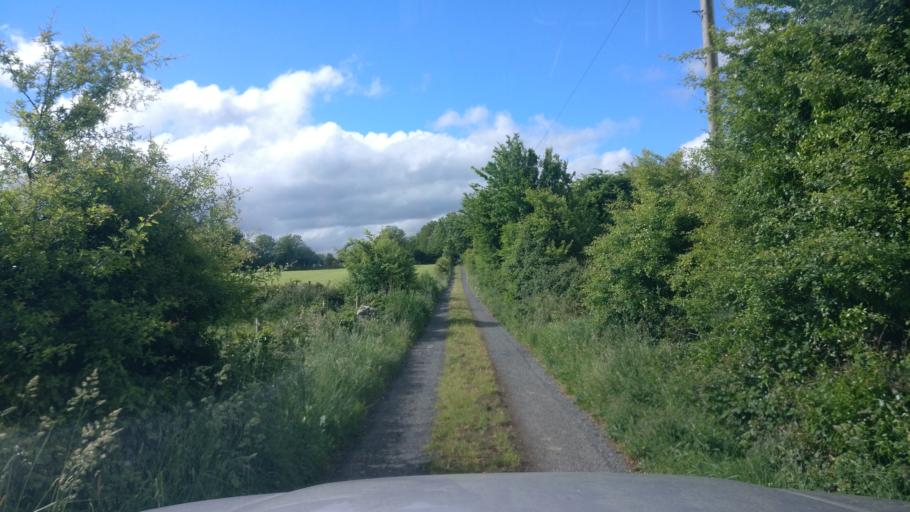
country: IE
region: Connaught
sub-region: County Galway
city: Loughrea
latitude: 53.2393
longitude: -8.6017
